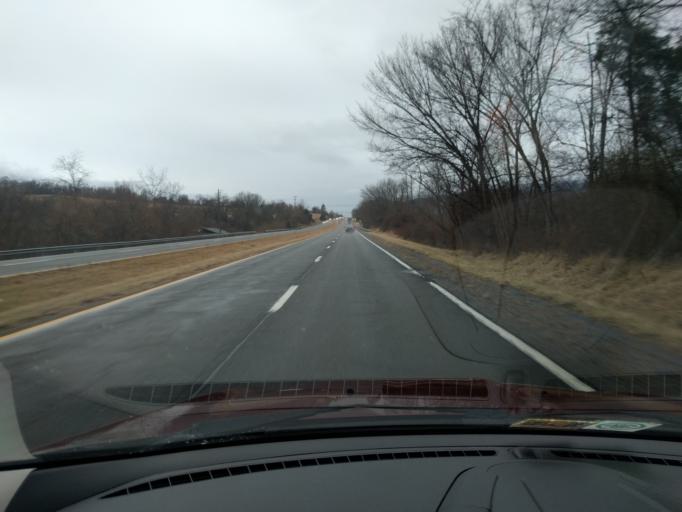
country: US
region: Virginia
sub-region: Giles County
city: Pembroke
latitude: 37.3081
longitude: -80.5763
